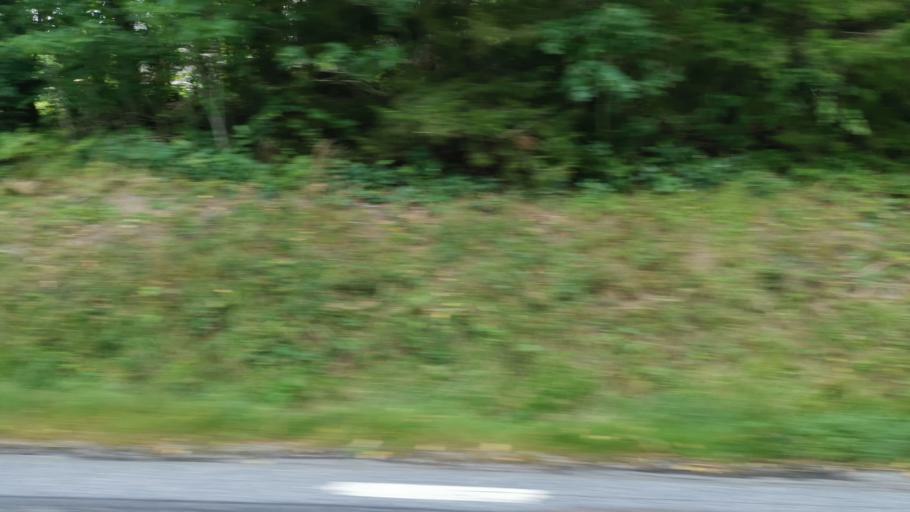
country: SE
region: Vaestra Goetaland
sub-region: Lysekils Kommun
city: Brastad
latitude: 58.4669
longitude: 11.4486
